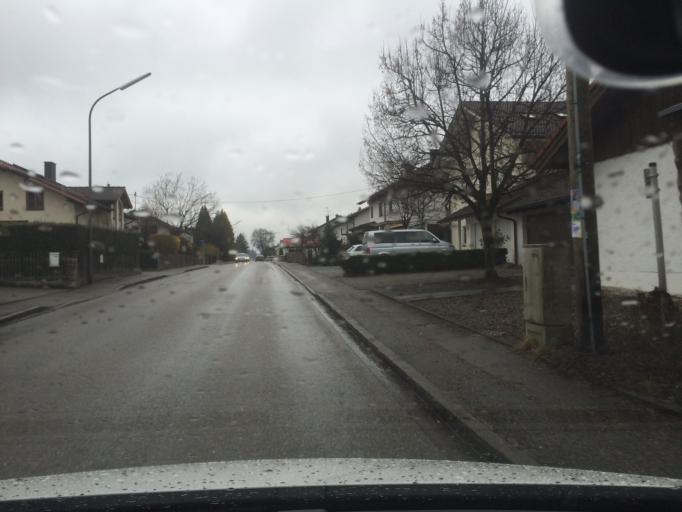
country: DE
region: Bavaria
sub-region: Upper Bavaria
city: Grosskarolinenfeld
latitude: 47.8846
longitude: 12.0764
